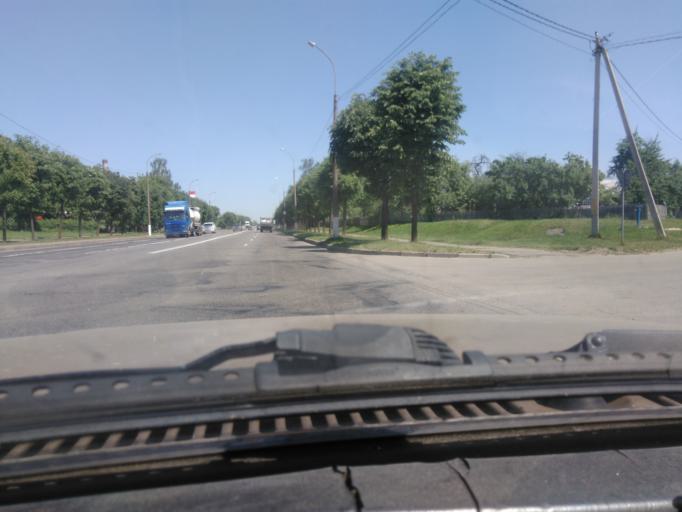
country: BY
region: Mogilev
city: Mahilyow
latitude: 53.9109
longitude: 30.3621
